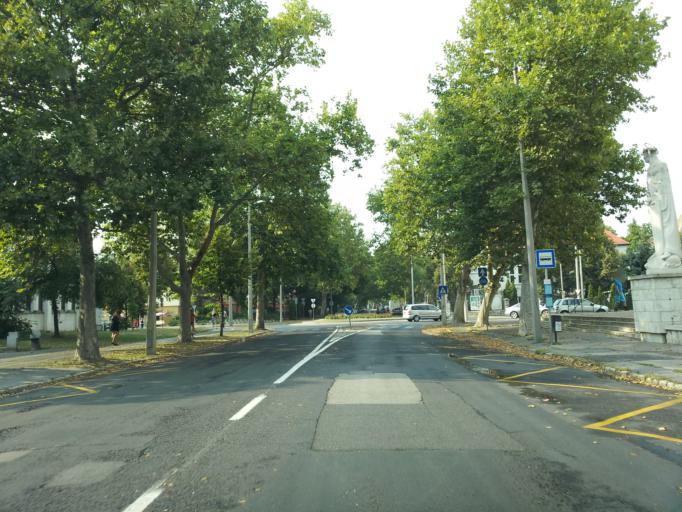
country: HU
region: Gyor-Moson-Sopron
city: Gyor
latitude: 47.6719
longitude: 17.6449
